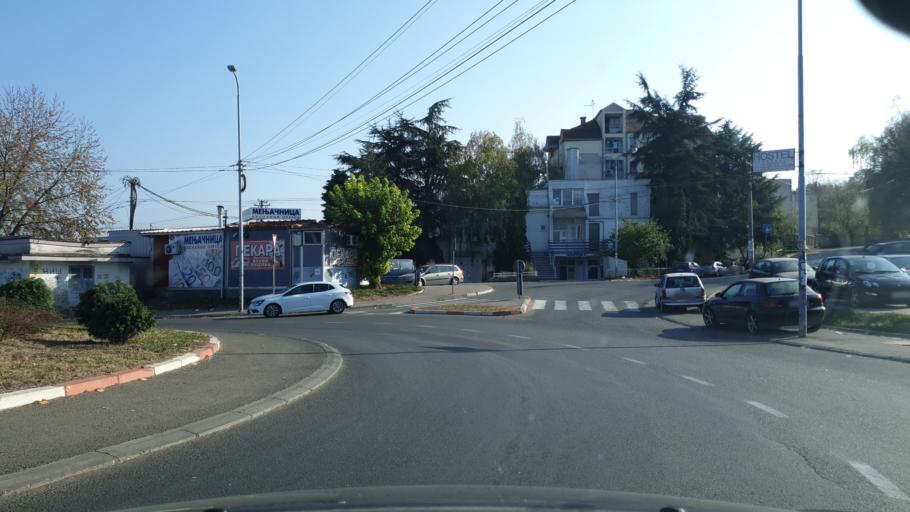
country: RS
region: Central Serbia
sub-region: Nisavski Okrug
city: Nis
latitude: 43.3152
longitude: 21.8639
